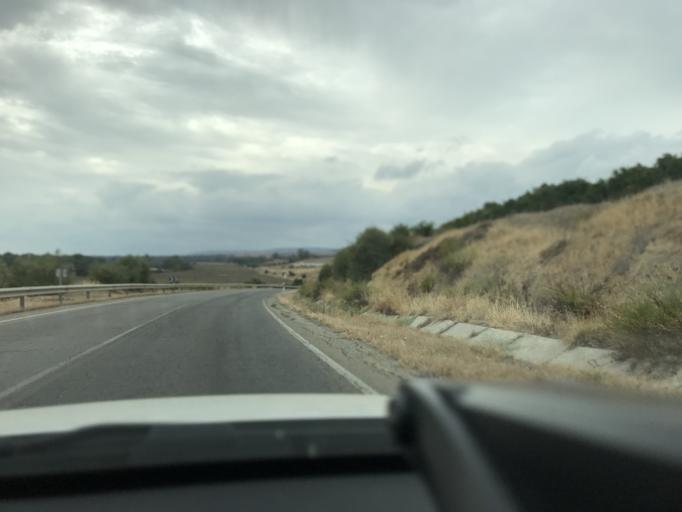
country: ES
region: Andalusia
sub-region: Provincia de Sevilla
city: Villanueva del Rio y Minas
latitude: 37.6347
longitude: -5.7070
